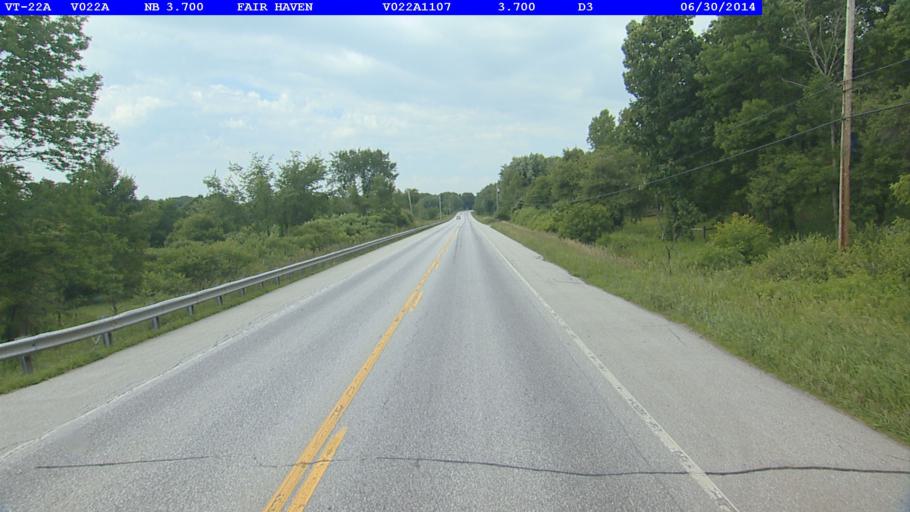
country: US
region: Vermont
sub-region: Rutland County
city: Fair Haven
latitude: 43.6178
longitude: -73.2954
